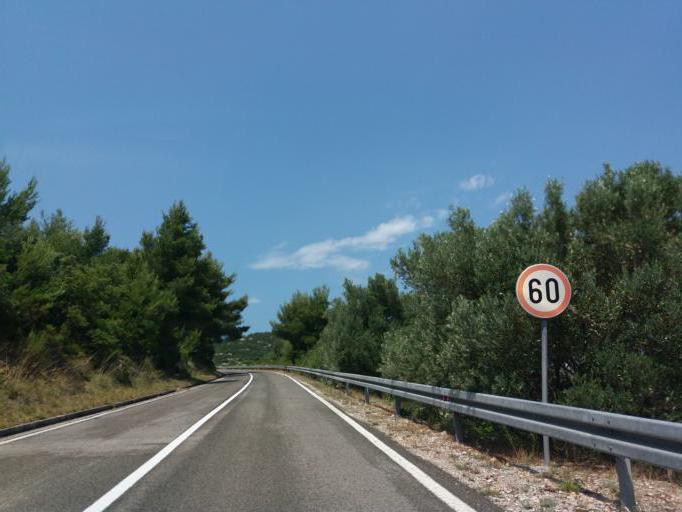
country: HR
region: Zadarska
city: Sali
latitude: 43.9724
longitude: 15.0989
